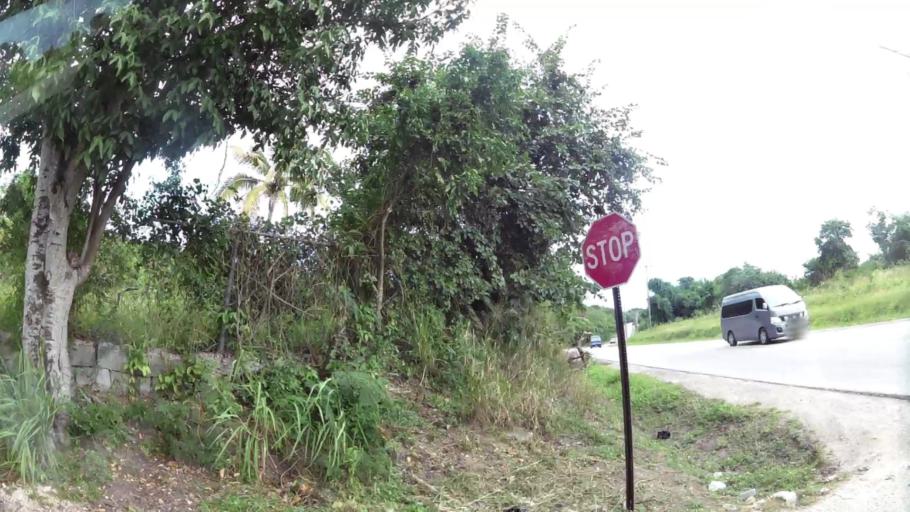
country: AG
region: Saint John
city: Potters Village
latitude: 17.0871
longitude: -61.8110
